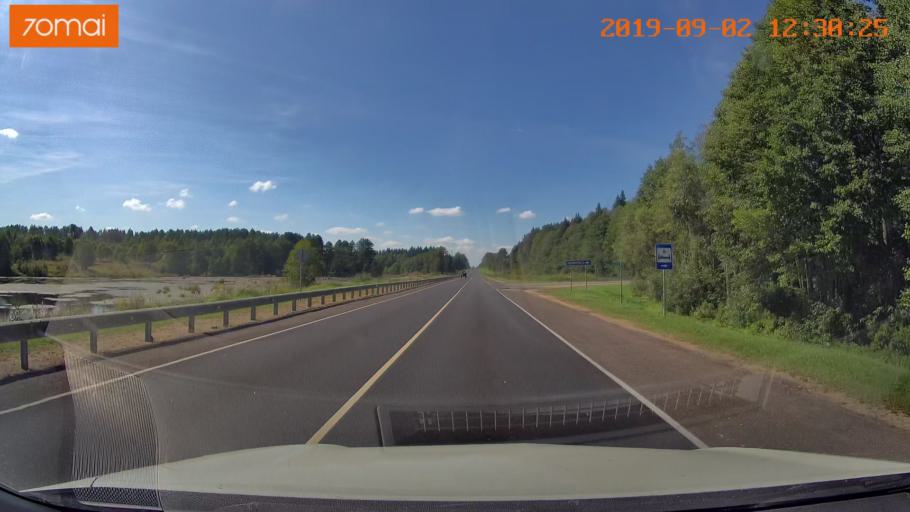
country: RU
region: Smolensk
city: Shumyachi
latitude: 53.8322
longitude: 32.4750
